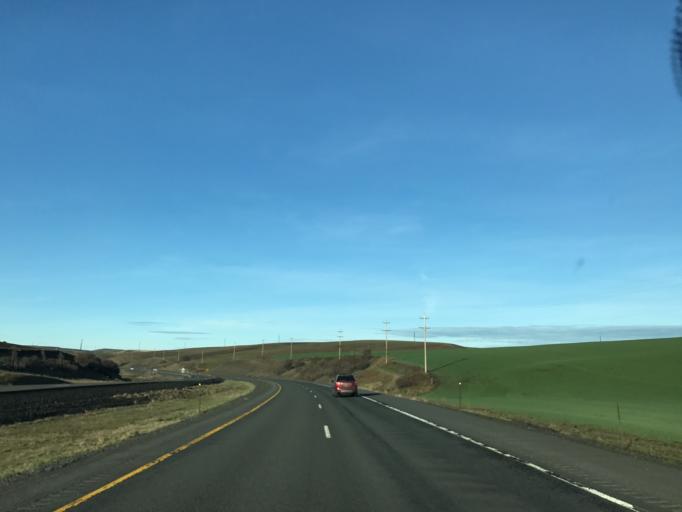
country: US
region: Idaho
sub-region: Nez Perce County
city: Lewiston
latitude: 46.4894
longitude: -117.0262
